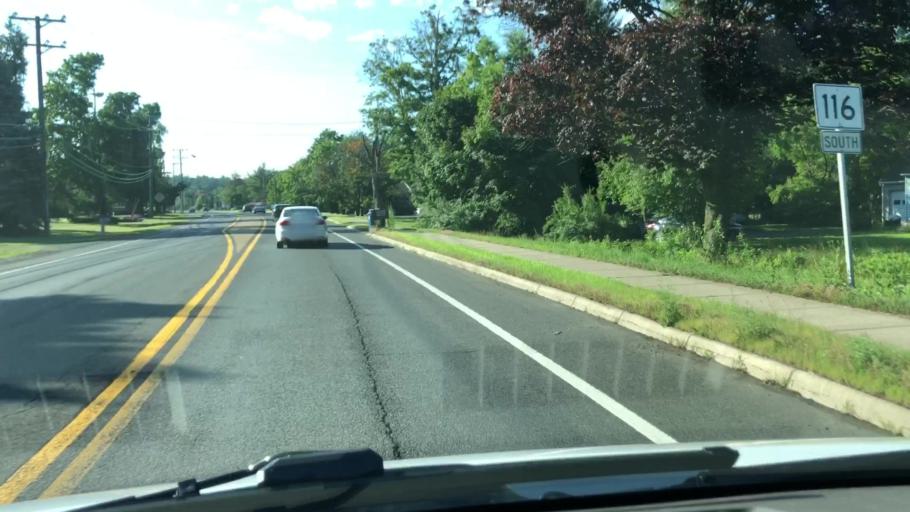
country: US
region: Massachusetts
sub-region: Franklin County
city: South Deerfield
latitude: 42.4541
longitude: -72.5661
